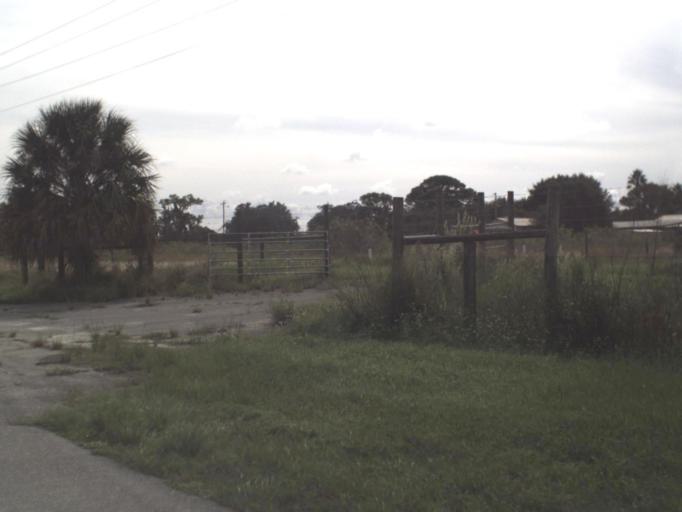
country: US
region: Florida
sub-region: Highlands County
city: Placid Lakes
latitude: 27.2087
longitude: -81.3988
